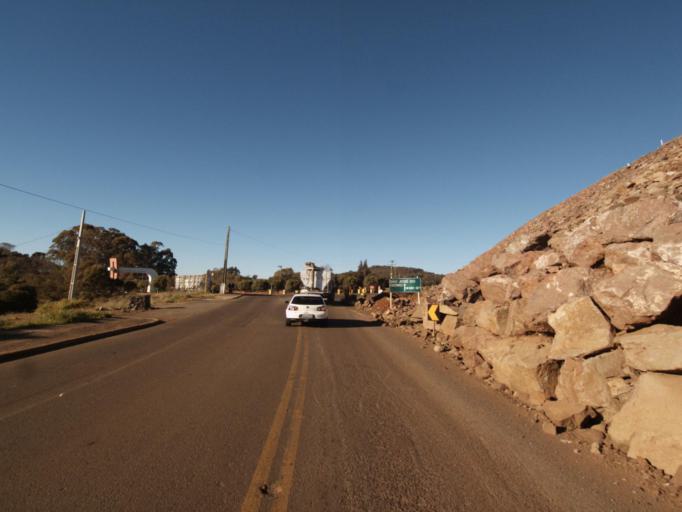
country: AR
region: Misiones
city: Bernardo de Irigoyen
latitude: -26.4540
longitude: -53.5102
